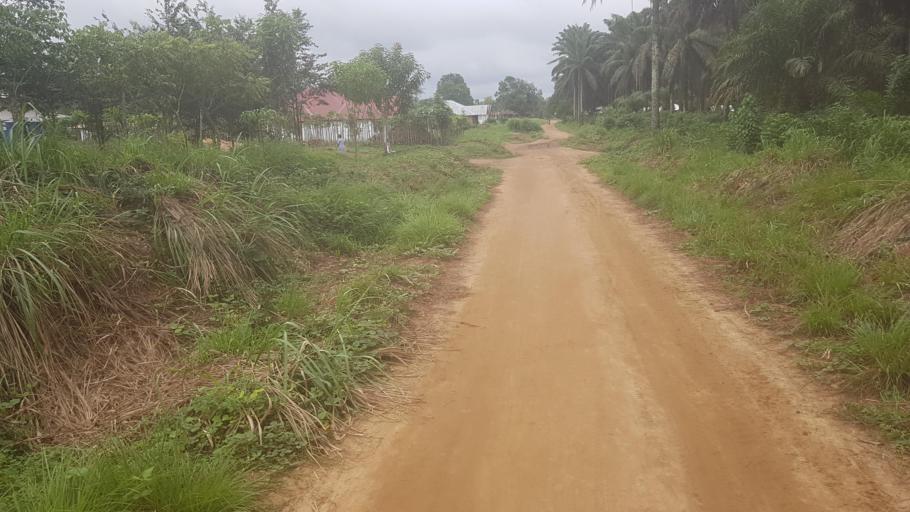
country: SL
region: Southern Province
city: Sumbuya
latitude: 7.5626
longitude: -12.1548
